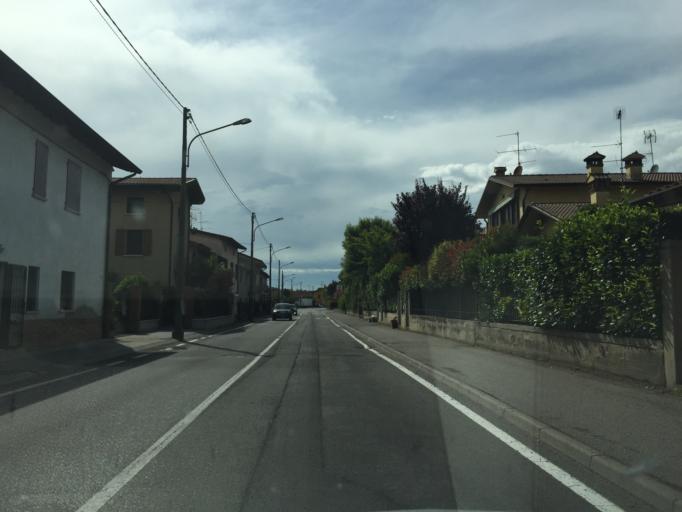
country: IT
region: Lombardy
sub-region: Provincia di Brescia
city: Poncarale
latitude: 45.4582
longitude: 10.1930
